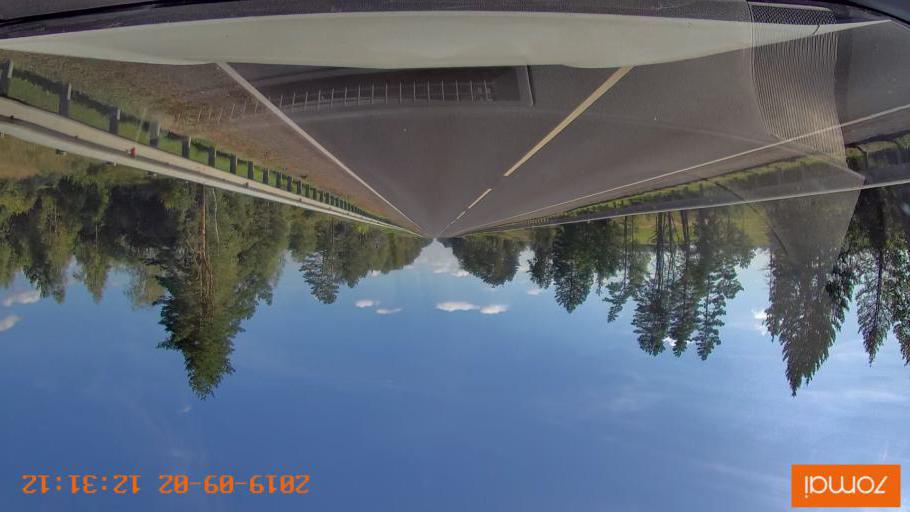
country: RU
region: Smolensk
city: Shumyachi
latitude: 53.8263
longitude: 32.4559
